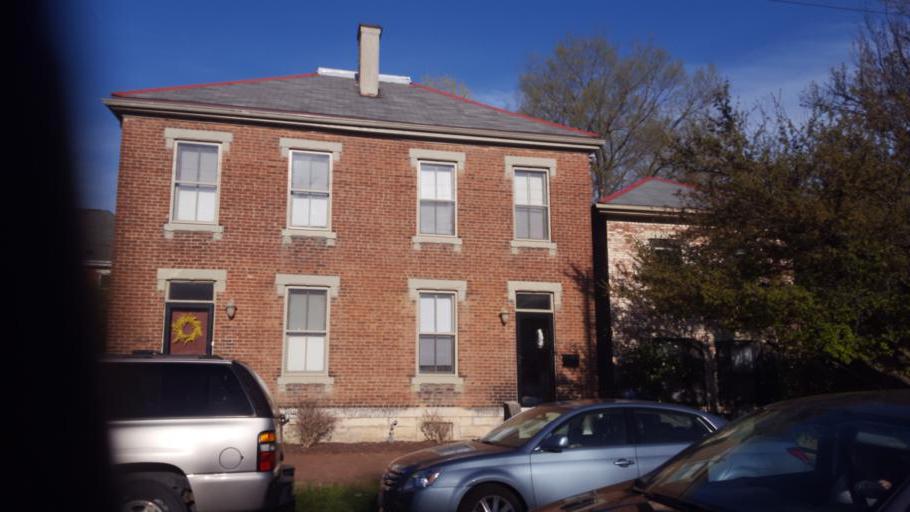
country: US
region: Ohio
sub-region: Franklin County
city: Columbus
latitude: 39.9456
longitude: -82.9947
